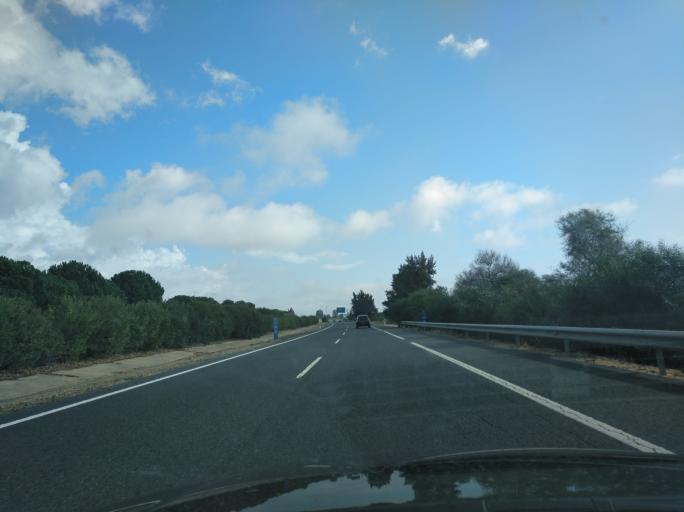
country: ES
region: Andalusia
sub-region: Provincia de Huelva
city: Cartaya
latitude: 37.3225
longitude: -7.0865
